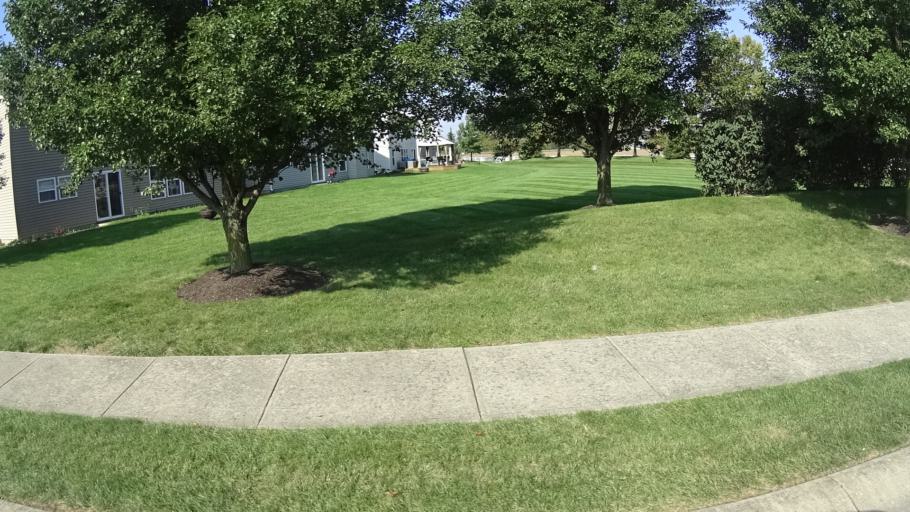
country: US
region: Indiana
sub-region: Madison County
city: Ingalls
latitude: 39.9872
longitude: -85.8479
